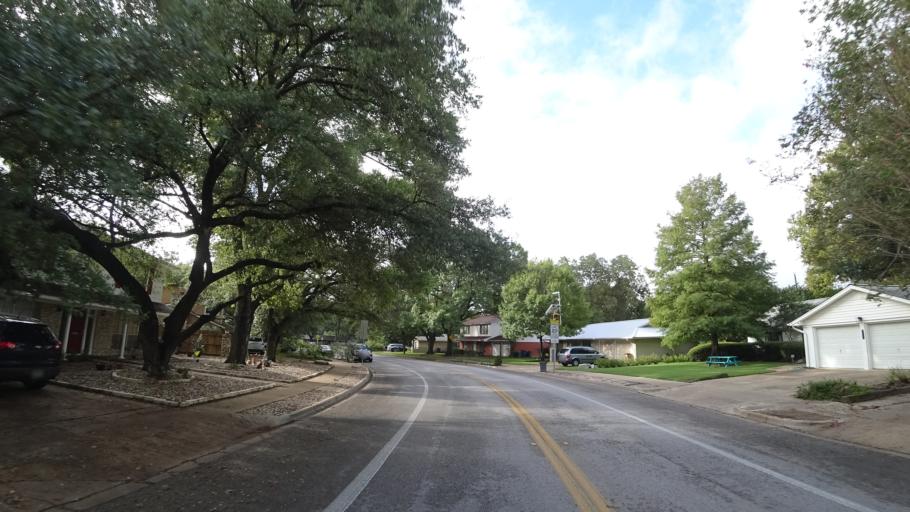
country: US
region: Texas
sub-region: Travis County
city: West Lake Hills
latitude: 30.3476
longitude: -97.7460
